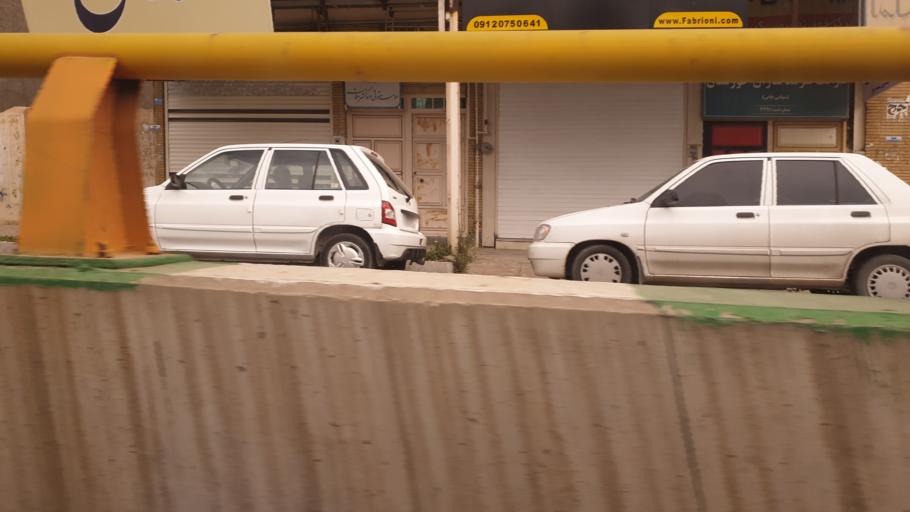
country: IR
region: Khuzestan
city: Dezful
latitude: 32.3812
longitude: 48.4061
